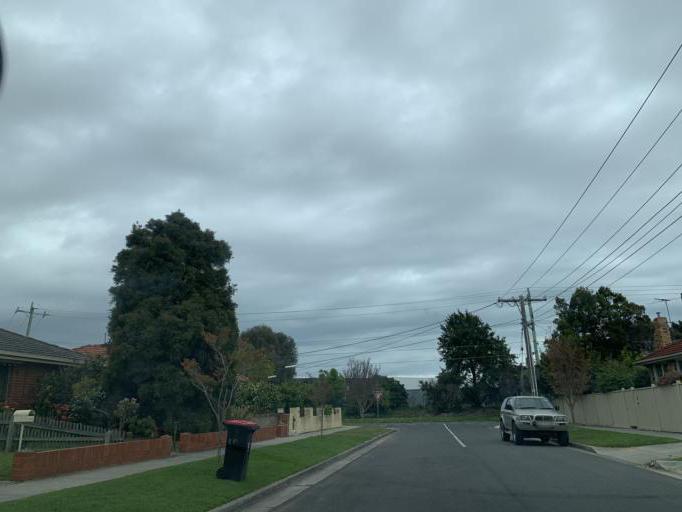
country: AU
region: Victoria
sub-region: Kingston
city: Mentone
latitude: -37.9738
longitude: 145.0682
